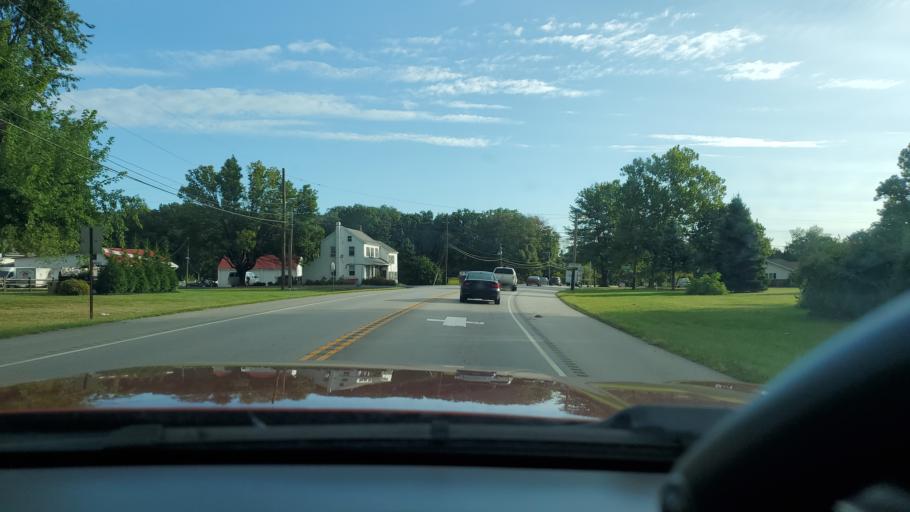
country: US
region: Pennsylvania
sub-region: Montgomery County
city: Harleysville
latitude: 40.2904
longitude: -75.3836
